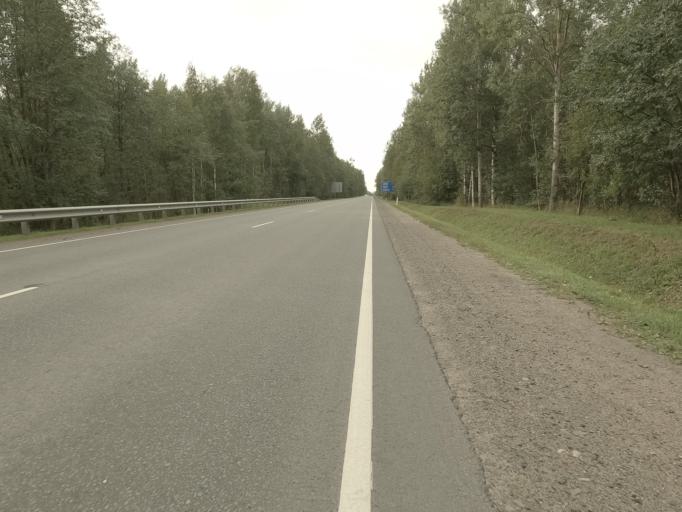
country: RU
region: Leningrad
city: Kirovsk
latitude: 59.8473
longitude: 31.0368
